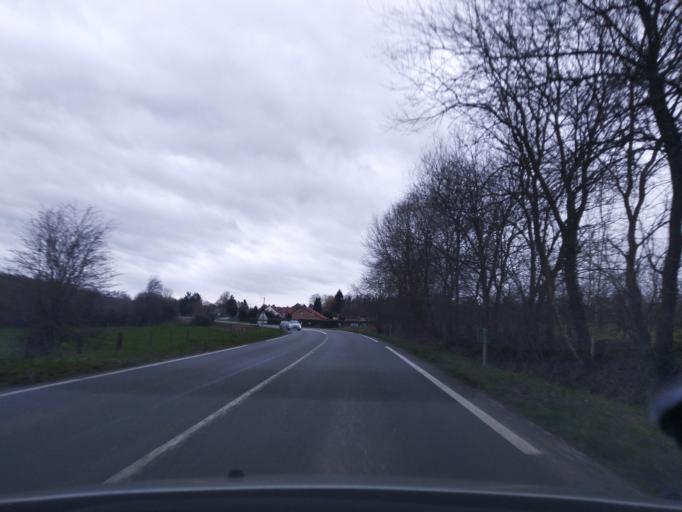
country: FR
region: Nord-Pas-de-Calais
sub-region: Departement du Pas-de-Calais
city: Camblain-Chatelain
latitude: 50.4413
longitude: 2.4565
